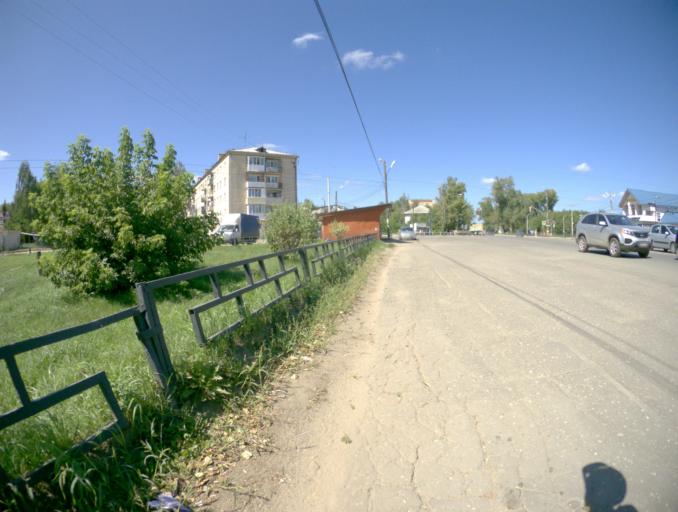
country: RU
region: Nizjnij Novgorod
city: Bor
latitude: 56.3551
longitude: 44.0732
